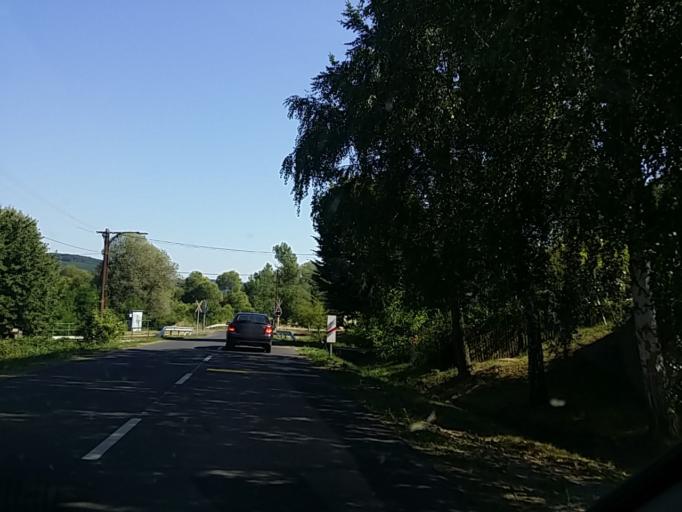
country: HU
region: Nograd
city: Szecseny
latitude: 48.1871
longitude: 19.5271
